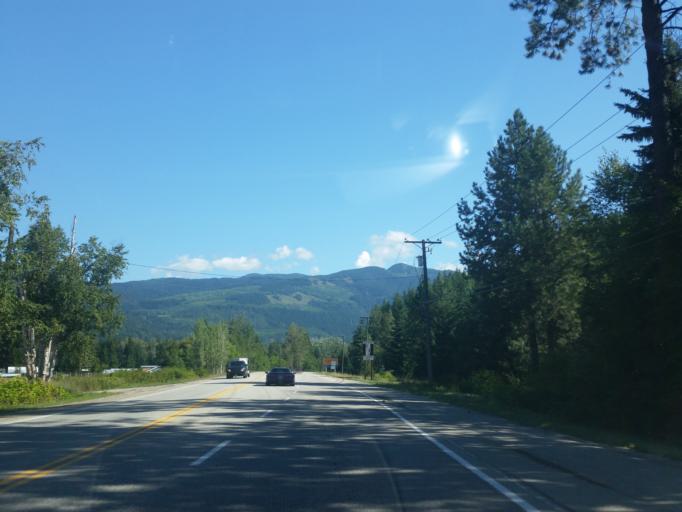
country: CA
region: British Columbia
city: Sicamous
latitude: 50.8522
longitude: -118.9455
